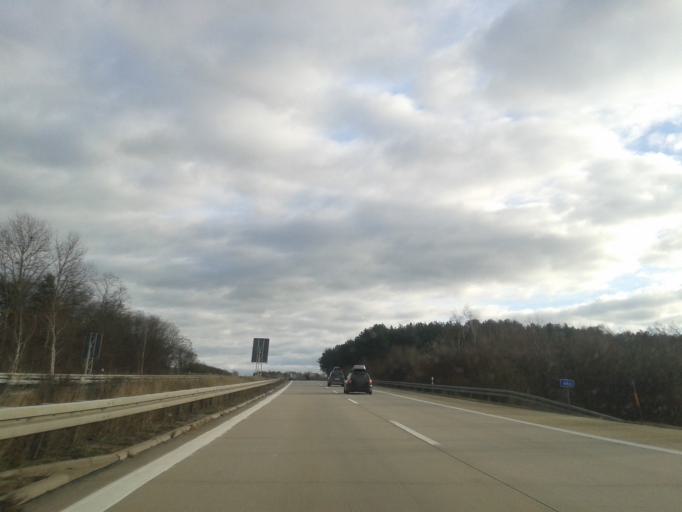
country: DE
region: Saxony
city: Guttau
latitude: 51.2100
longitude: 14.5788
